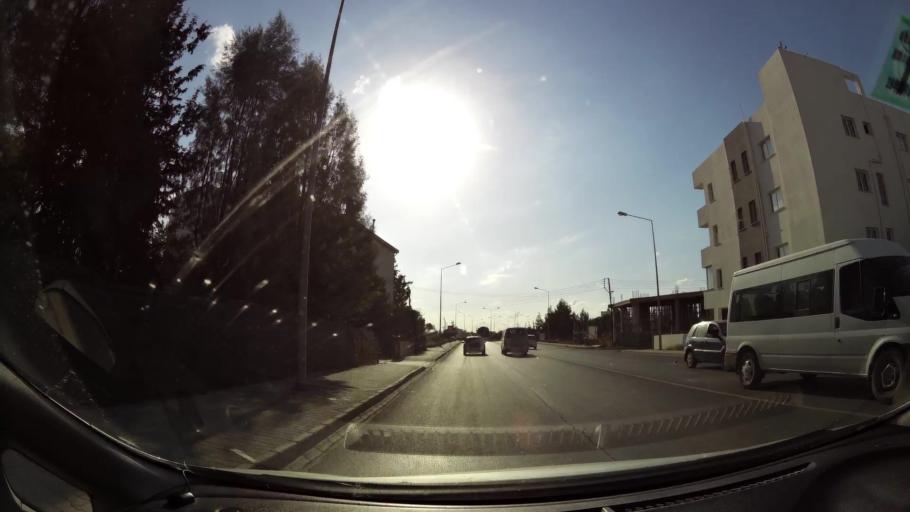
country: CY
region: Lefkosia
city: Nicosia
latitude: 35.1999
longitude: 33.3593
